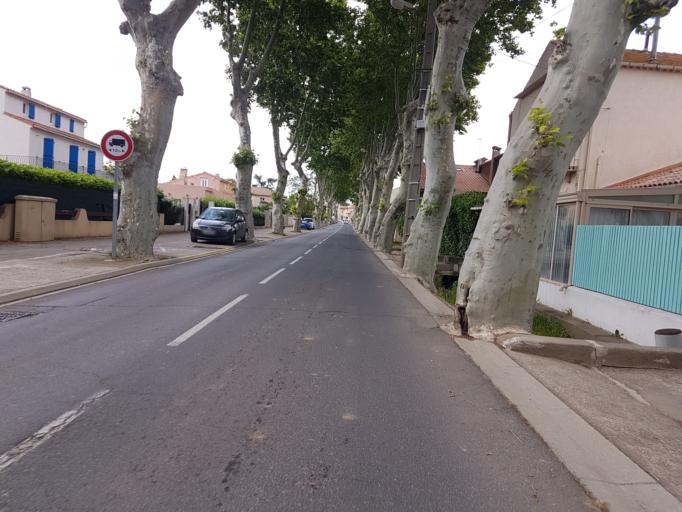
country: FR
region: Languedoc-Roussillon
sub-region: Departement de l'Herault
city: Cers
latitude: 43.3209
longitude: 3.3037
